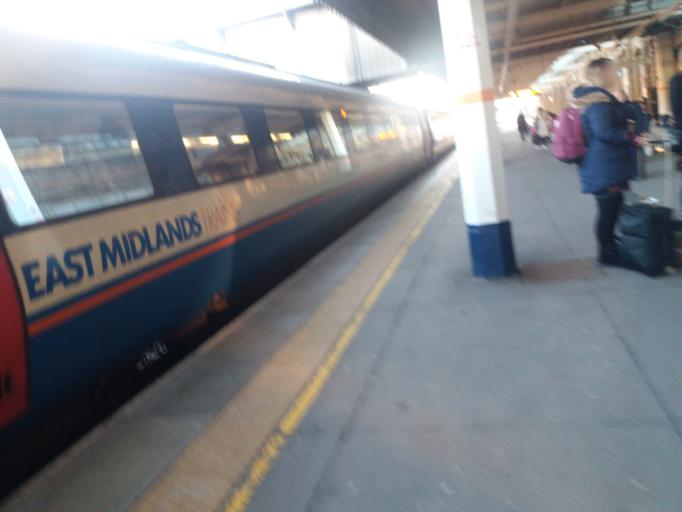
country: GB
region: England
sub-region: Sheffield
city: Sheffield
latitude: 53.3782
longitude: -1.4619
